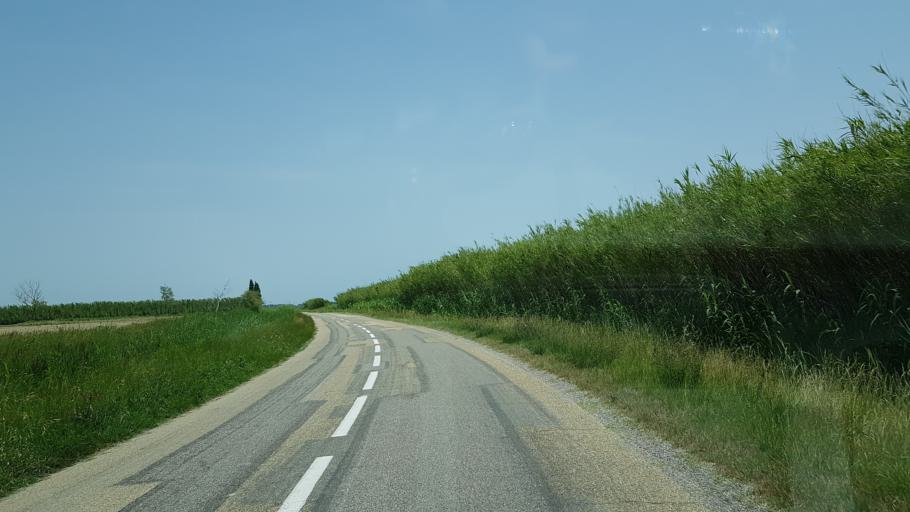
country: FR
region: Provence-Alpes-Cote d'Azur
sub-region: Departement des Bouches-du-Rhone
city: Port-Saint-Louis-du-Rhone
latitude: 43.4278
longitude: 4.7019
